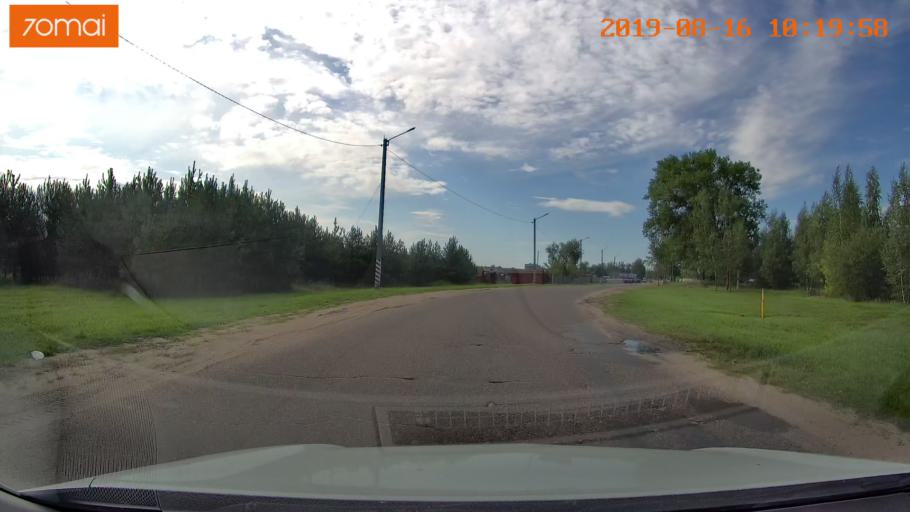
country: BY
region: Mogilev
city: Asipovichy
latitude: 53.3045
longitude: 28.6640
